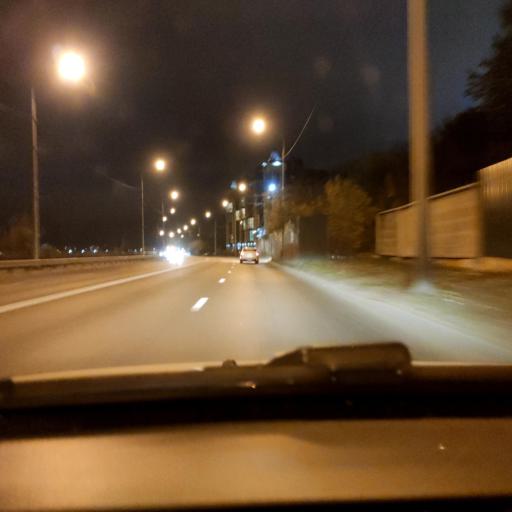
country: RU
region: Voronezj
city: Voronezh
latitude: 51.6833
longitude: 39.2283
